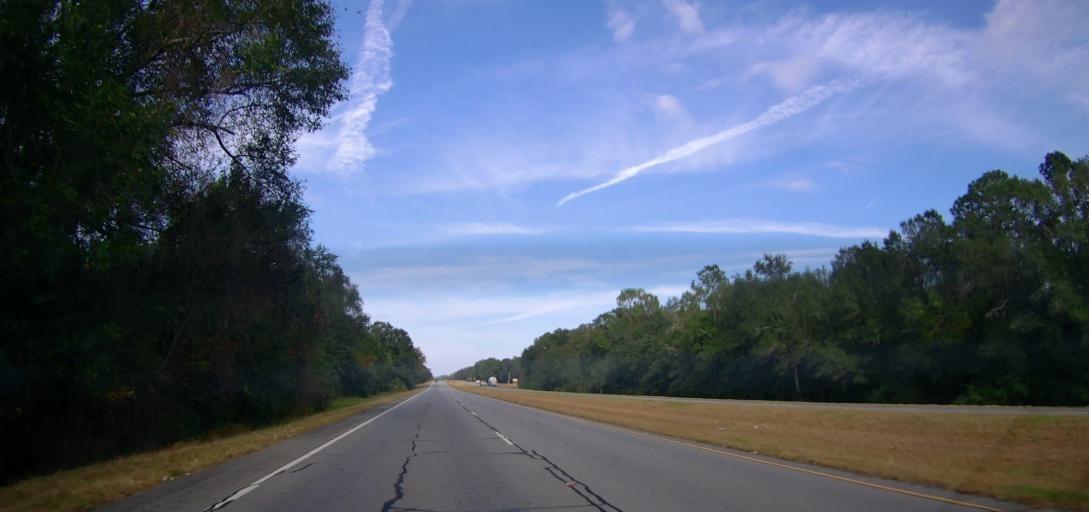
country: US
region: Georgia
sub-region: Mitchell County
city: Camilla
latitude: 31.2979
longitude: -84.1823
